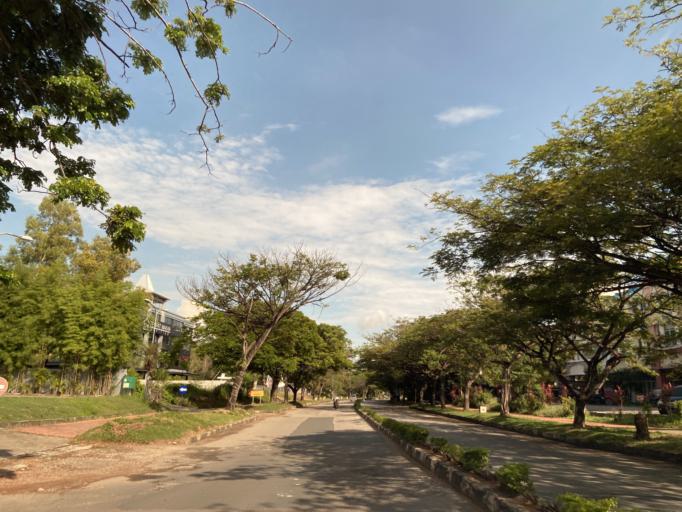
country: SG
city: Singapore
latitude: 1.1277
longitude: 104.0514
